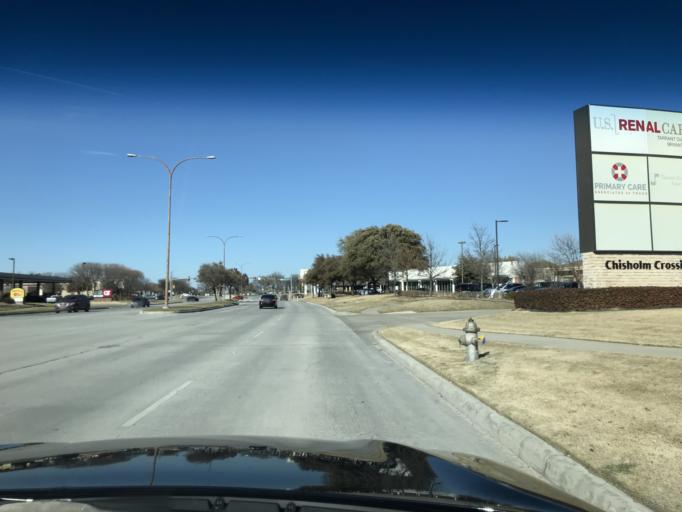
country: US
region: Texas
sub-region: Tarrant County
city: Benbrook
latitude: 32.6648
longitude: -97.4207
